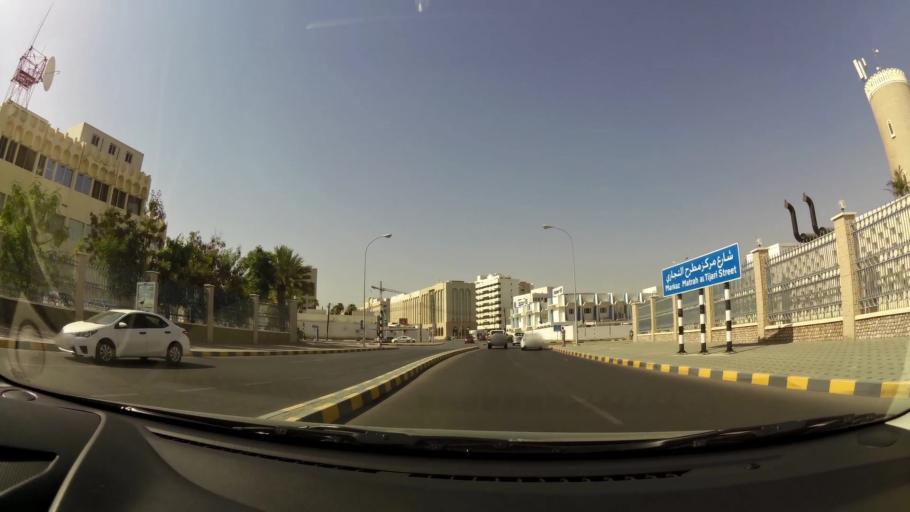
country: OM
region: Muhafazat Masqat
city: Muscat
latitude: 23.6043
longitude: 58.5464
